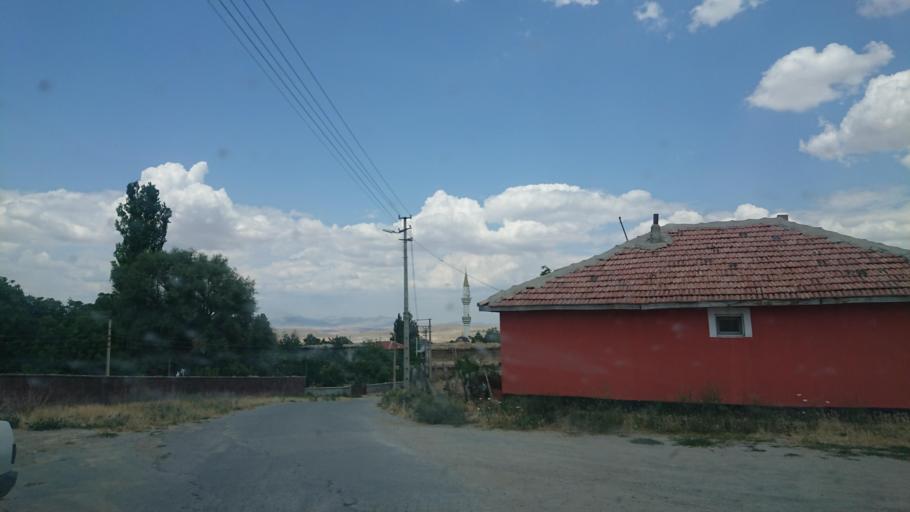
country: TR
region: Aksaray
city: Sariyahsi
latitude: 38.9581
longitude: 33.8844
